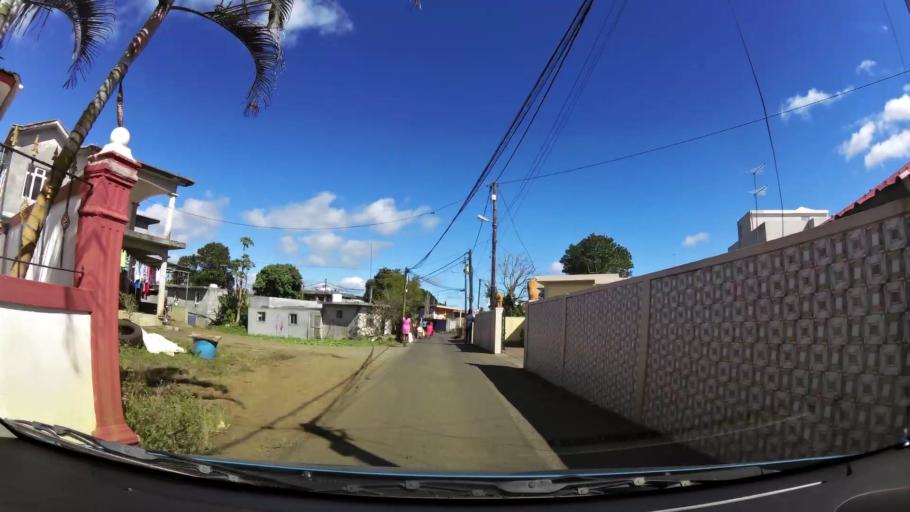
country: MU
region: Plaines Wilhems
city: Vacoas
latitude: -20.3166
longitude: 57.4901
